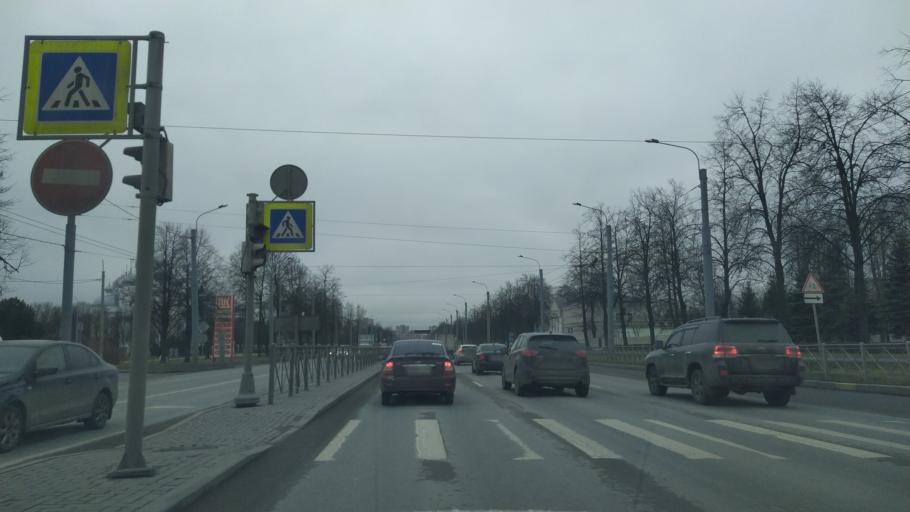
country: RU
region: Leningrad
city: Kalininskiy
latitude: 59.9832
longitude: 30.4243
